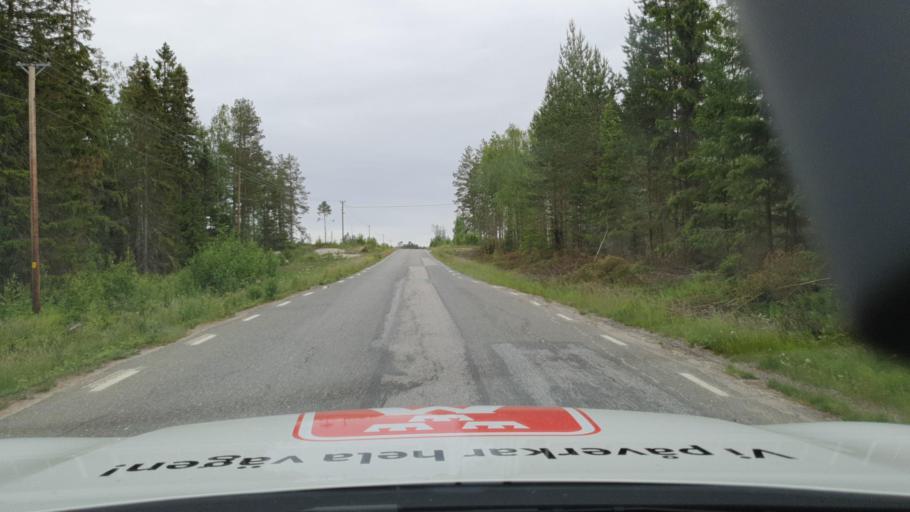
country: SE
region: Vaesterbotten
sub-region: Nordmalings Kommun
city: Nordmaling
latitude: 63.4549
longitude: 19.4673
